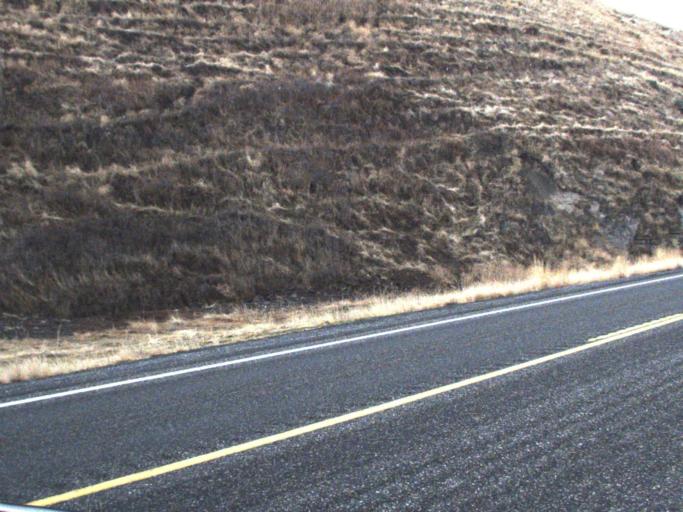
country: US
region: Washington
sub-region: Garfield County
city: Pomeroy
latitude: 46.4360
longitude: -117.3485
